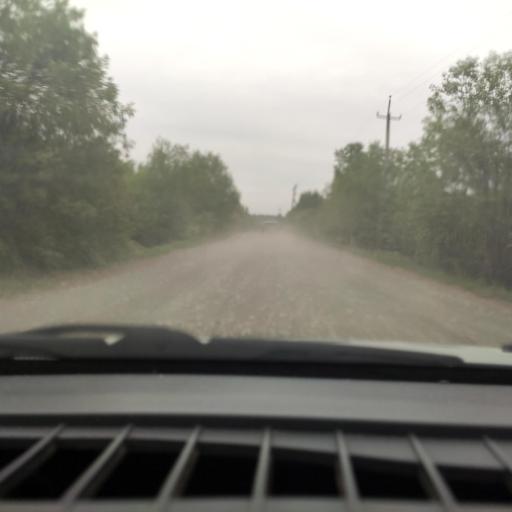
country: RU
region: Perm
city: Novyye Lyady
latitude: 57.9099
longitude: 56.6531
